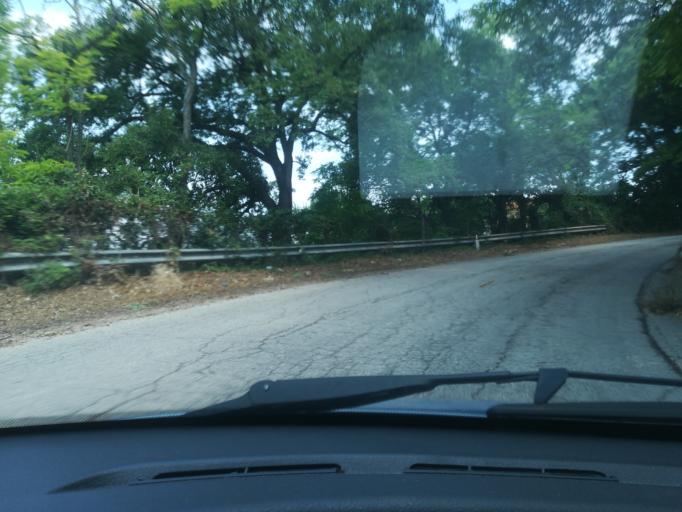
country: IT
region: The Marches
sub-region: Provincia di Macerata
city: Sforzacosta
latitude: 43.2647
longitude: 13.4385
